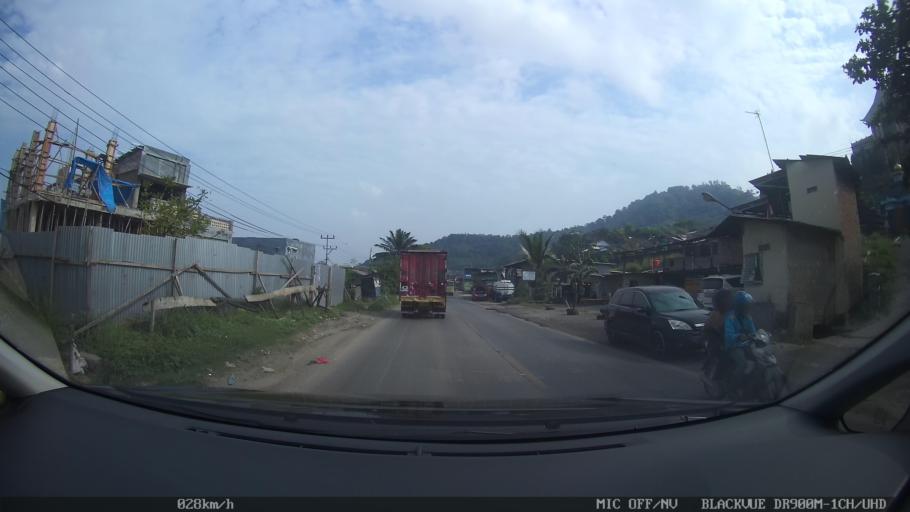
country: ID
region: Lampung
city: Panjang
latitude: -5.4655
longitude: 105.3221
